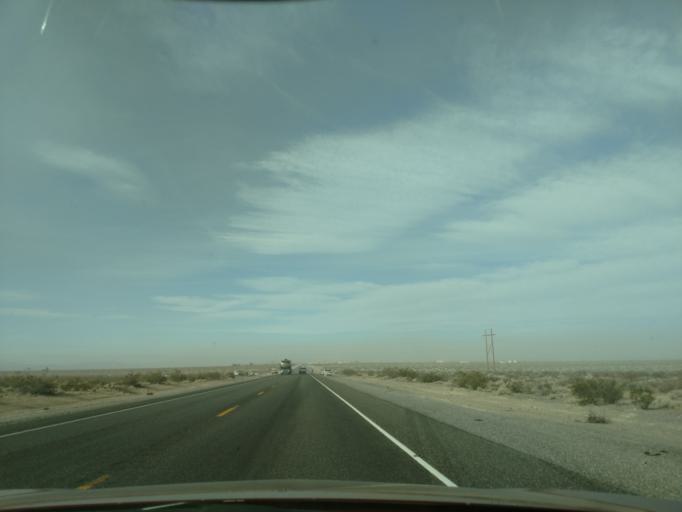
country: US
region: Nevada
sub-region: Nye County
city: Beatty
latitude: 36.6370
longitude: -116.3724
